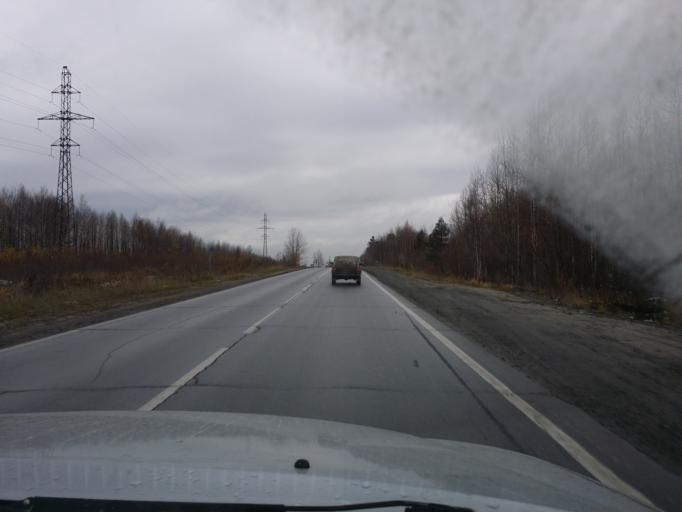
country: RU
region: Khanty-Mansiyskiy Avtonomnyy Okrug
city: Megion
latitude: 61.1057
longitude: 75.9244
